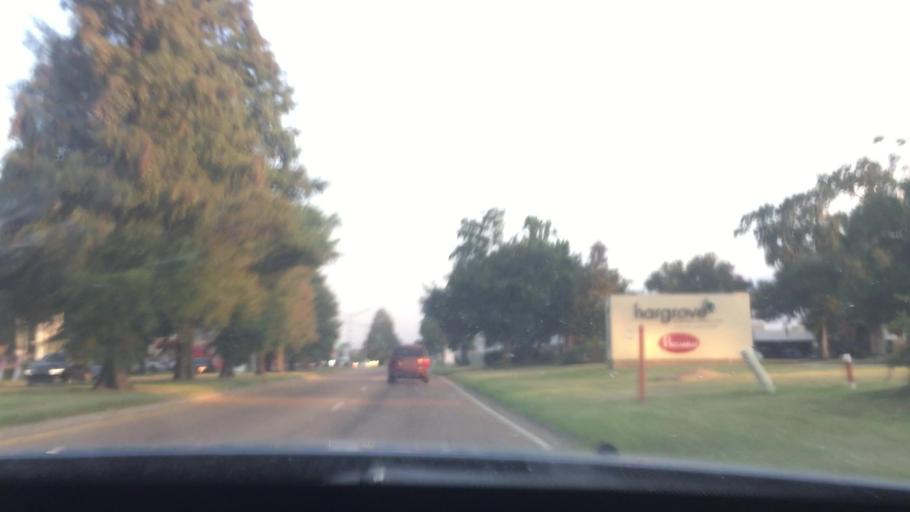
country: US
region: Louisiana
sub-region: East Baton Rouge Parish
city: Inniswold
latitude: 30.4158
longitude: -91.0517
